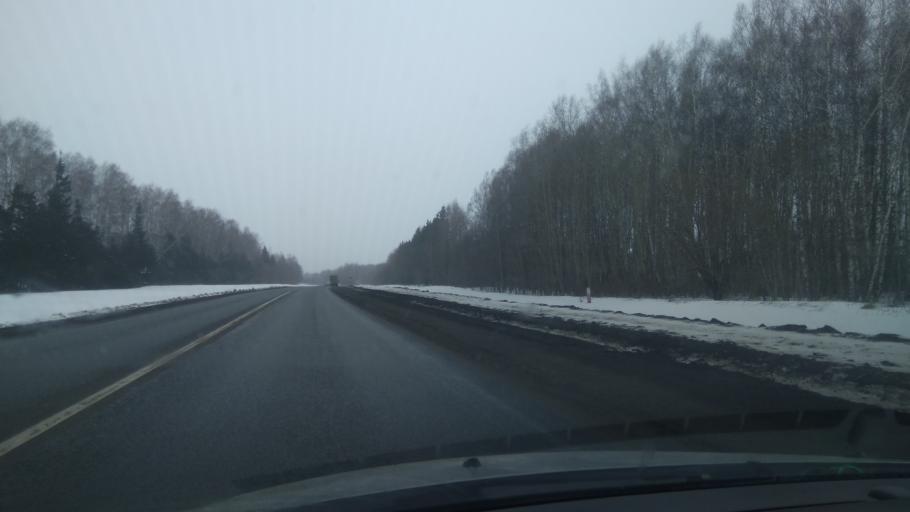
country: RU
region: Perm
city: Suksun
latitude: 57.1581
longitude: 57.2552
